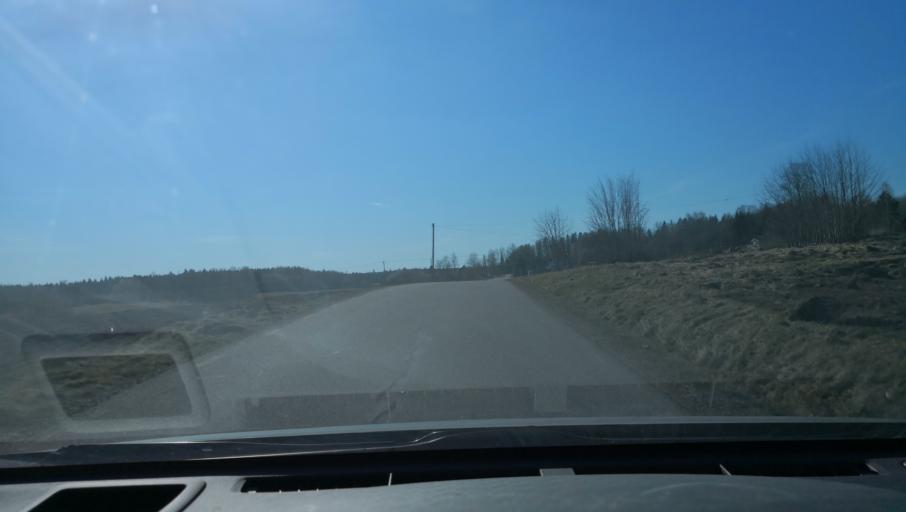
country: SE
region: Vaestmanland
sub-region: Sala Kommun
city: Sala
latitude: 60.0772
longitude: 16.4908
